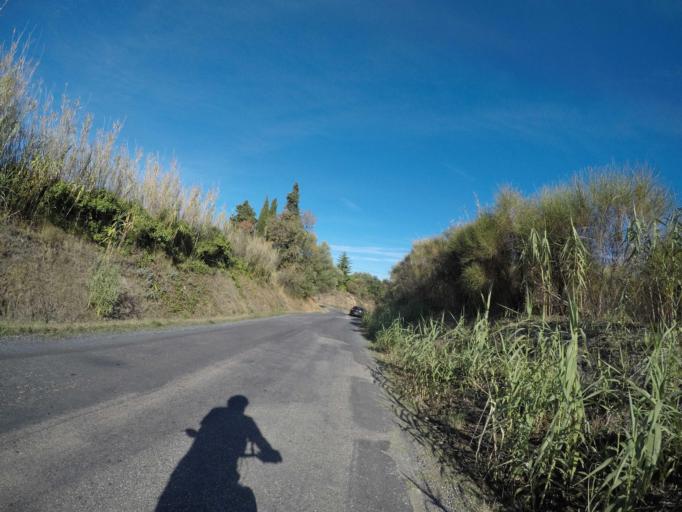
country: FR
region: Languedoc-Roussillon
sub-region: Departement des Pyrenees-Orientales
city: Trouillas
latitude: 42.6067
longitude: 2.8051
